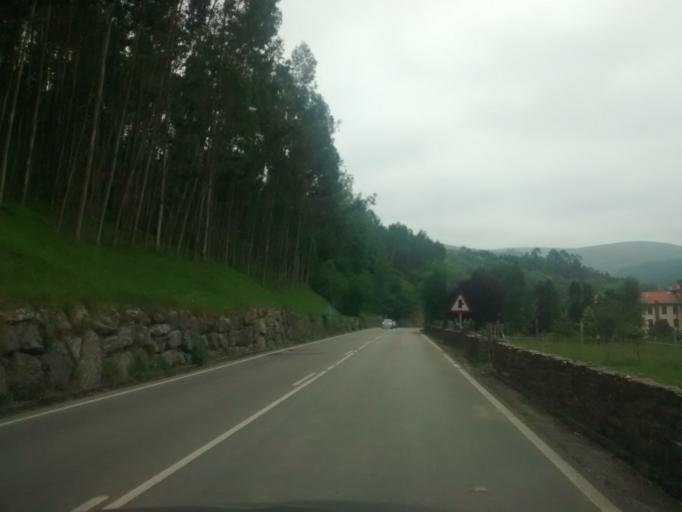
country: ES
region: Cantabria
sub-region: Provincia de Cantabria
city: Ruente
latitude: 43.2162
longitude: -4.3033
